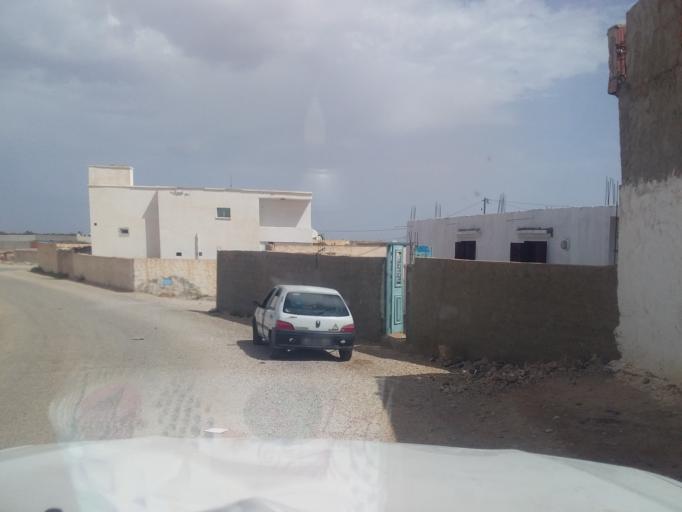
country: TN
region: Madanin
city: Medenine
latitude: 33.5868
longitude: 10.3219
